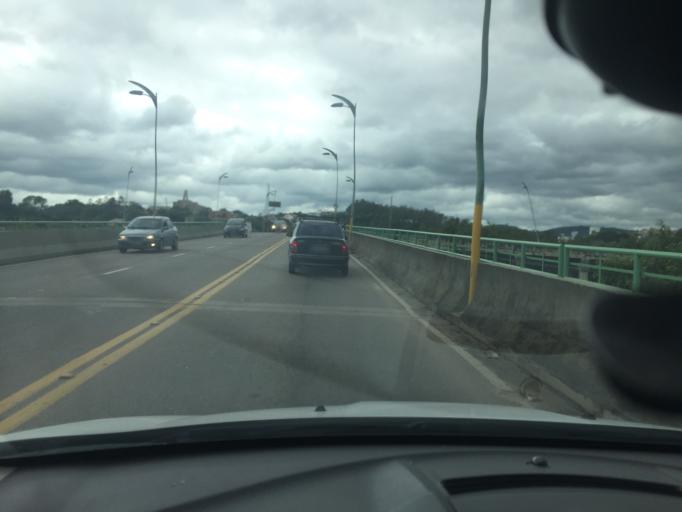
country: BR
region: Sao Paulo
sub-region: Varzea Paulista
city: Varzea Paulista
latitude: -23.2088
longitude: -46.8322
